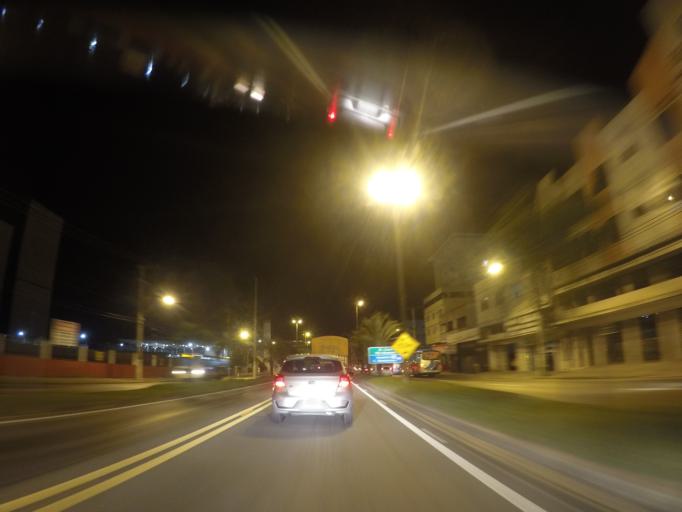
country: BR
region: Espirito Santo
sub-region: Linhares
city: Linhares
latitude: -19.3948
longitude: -40.0652
